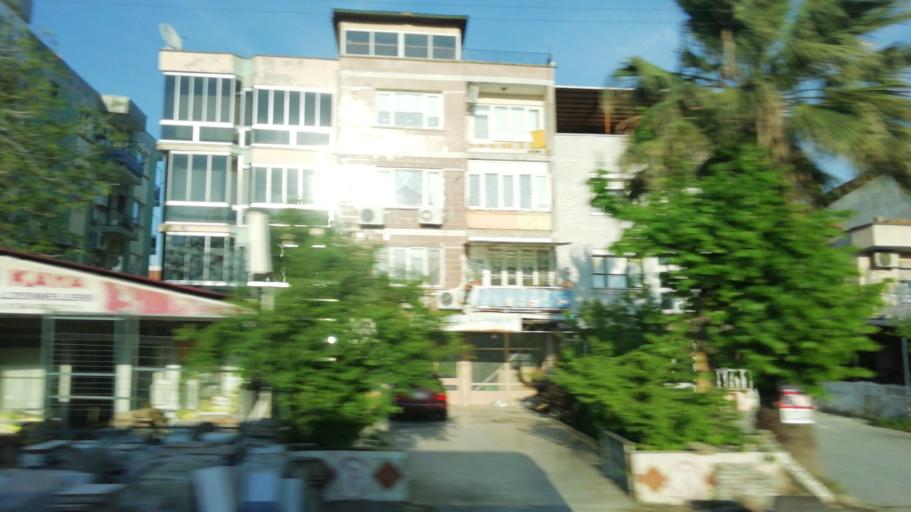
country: TR
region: Manisa
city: Akhisar
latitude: 38.9307
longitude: 27.8346
